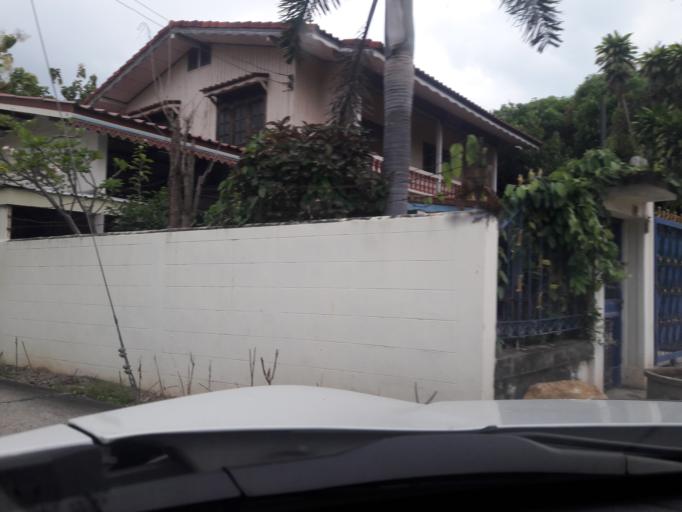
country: TH
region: Lop Buri
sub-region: Amphoe Tha Luang
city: Tha Luang
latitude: 15.0671
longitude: 101.1056
